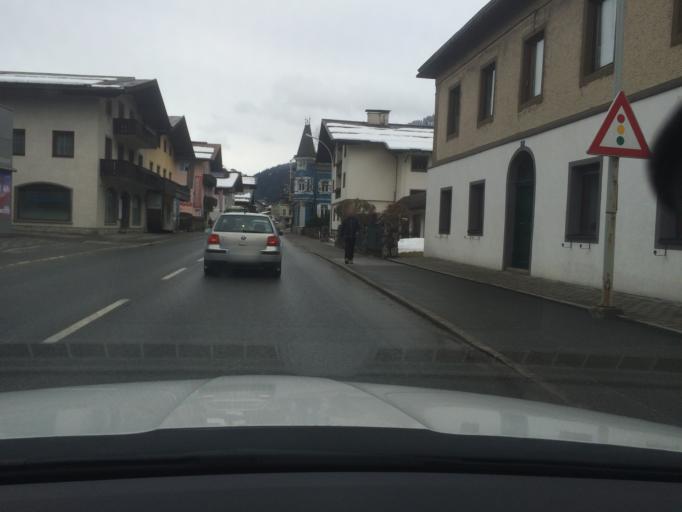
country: AT
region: Tyrol
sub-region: Politischer Bezirk Kitzbuhel
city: Kitzbuhel
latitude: 47.4521
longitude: 12.3891
